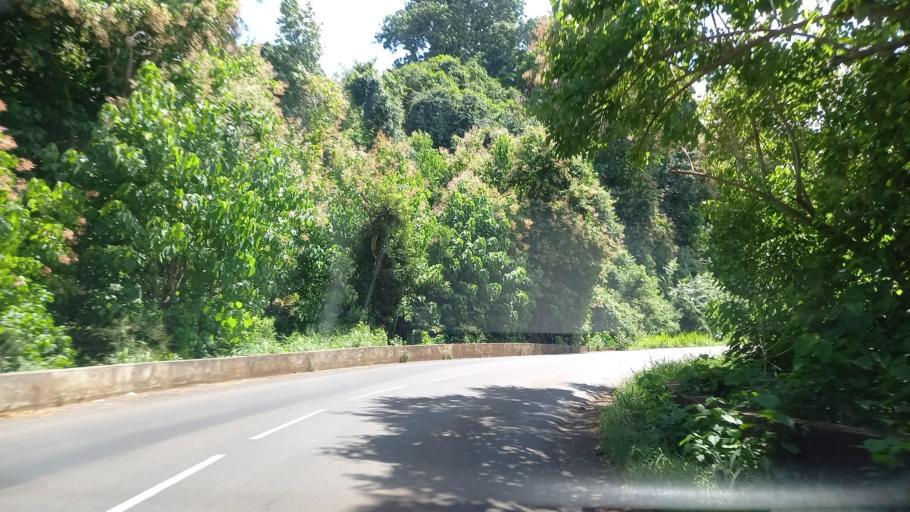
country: YT
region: Bandraboua
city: Bandraboua
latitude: -12.7196
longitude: 45.1289
